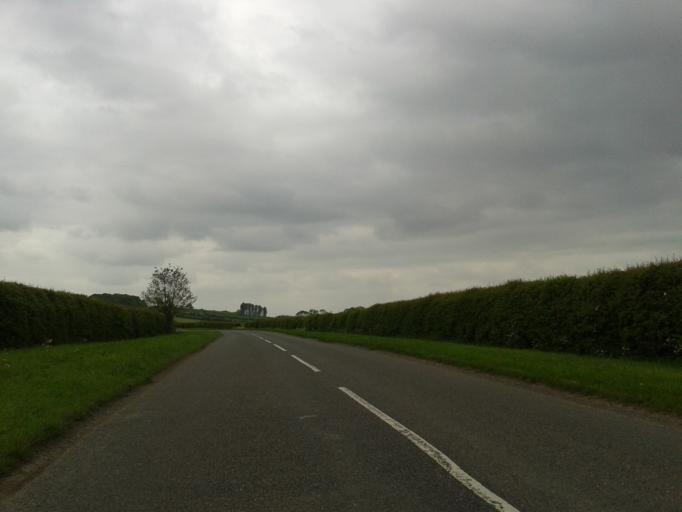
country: GB
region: England
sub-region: Northamptonshire
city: Corby
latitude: 52.5151
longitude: -0.7345
